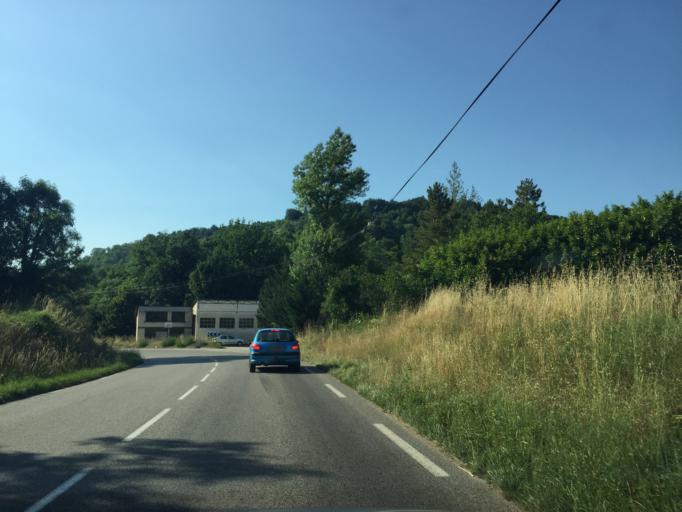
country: FR
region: Rhone-Alpes
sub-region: Departement de l'Isere
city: Saint-Just-de-Claix
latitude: 45.0579
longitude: 5.2843
